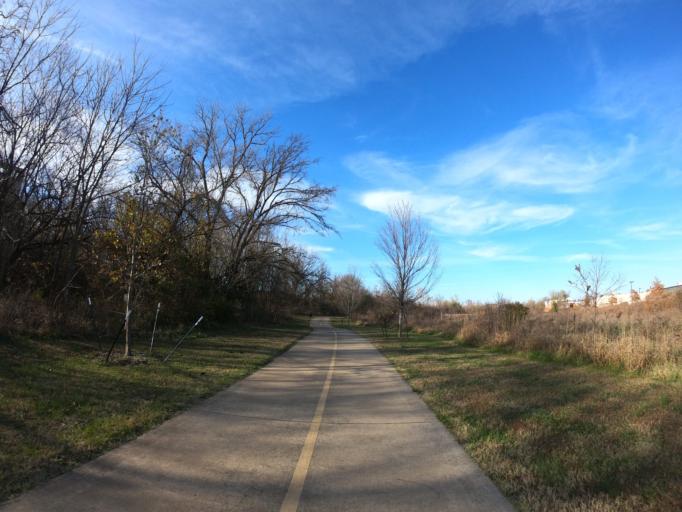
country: US
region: Arkansas
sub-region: Benton County
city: Rogers
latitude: 36.3094
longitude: -94.1809
